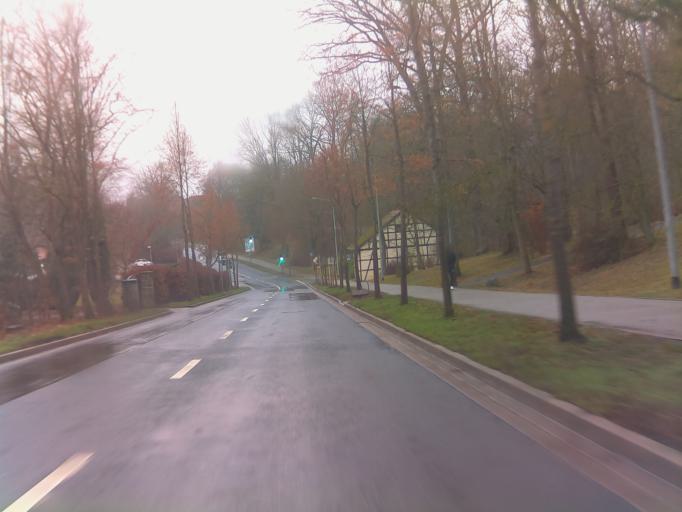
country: DE
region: Thuringia
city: Hildburghausen
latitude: 50.4229
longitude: 10.7418
